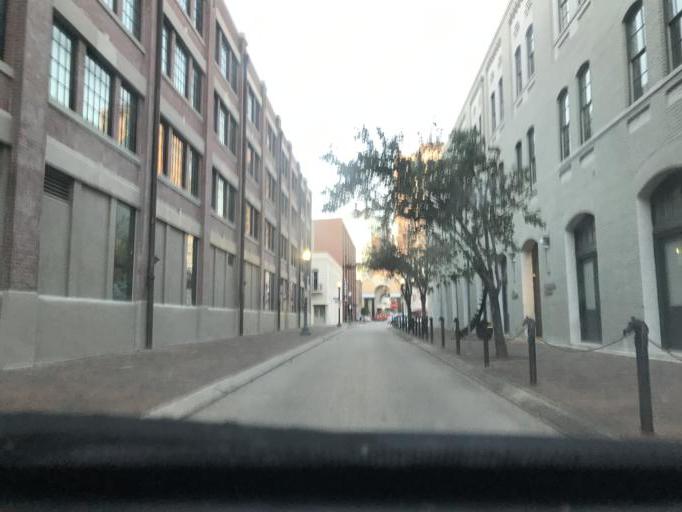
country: US
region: Louisiana
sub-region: Orleans Parish
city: New Orleans
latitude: 29.9456
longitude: -90.0666
